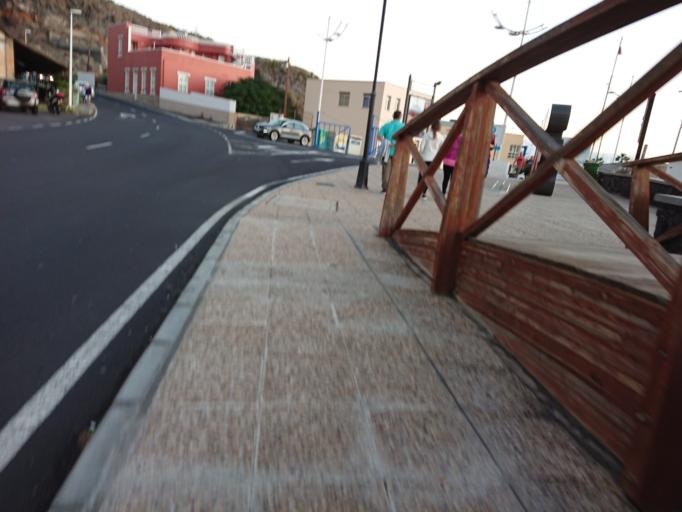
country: ES
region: Canary Islands
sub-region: Provincia de Santa Cruz de Tenerife
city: Tazacorte
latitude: 28.6480
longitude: -17.9441
